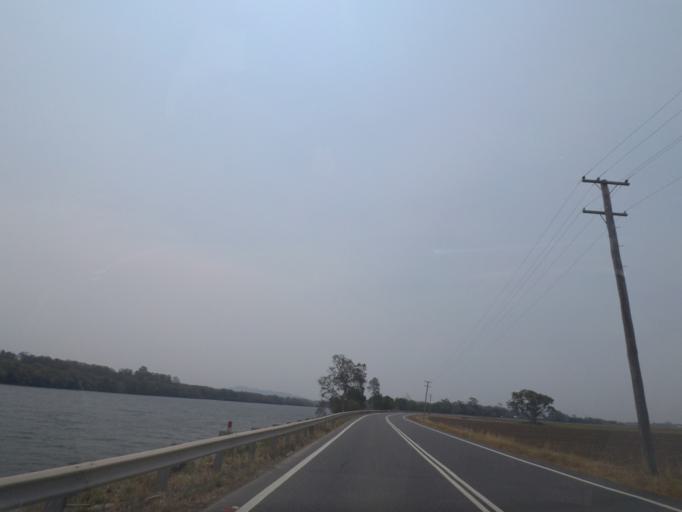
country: AU
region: New South Wales
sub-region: Richmond Valley
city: Evans Head
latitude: -28.9756
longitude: 153.4612
